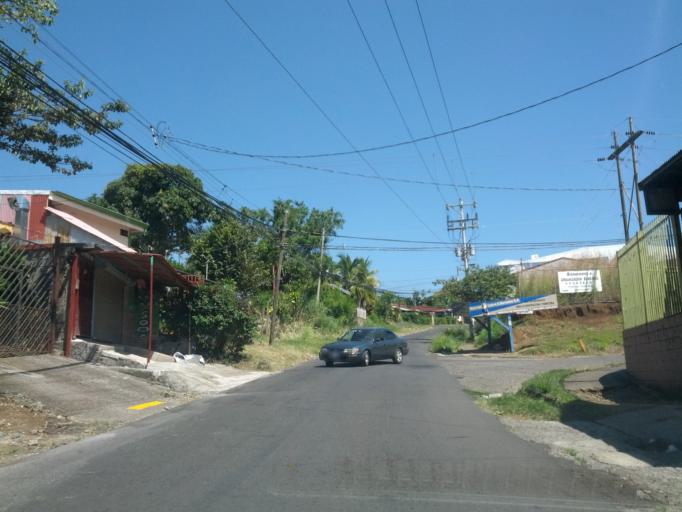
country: CR
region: Alajuela
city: Alajuela
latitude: 10.0133
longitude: -84.1845
